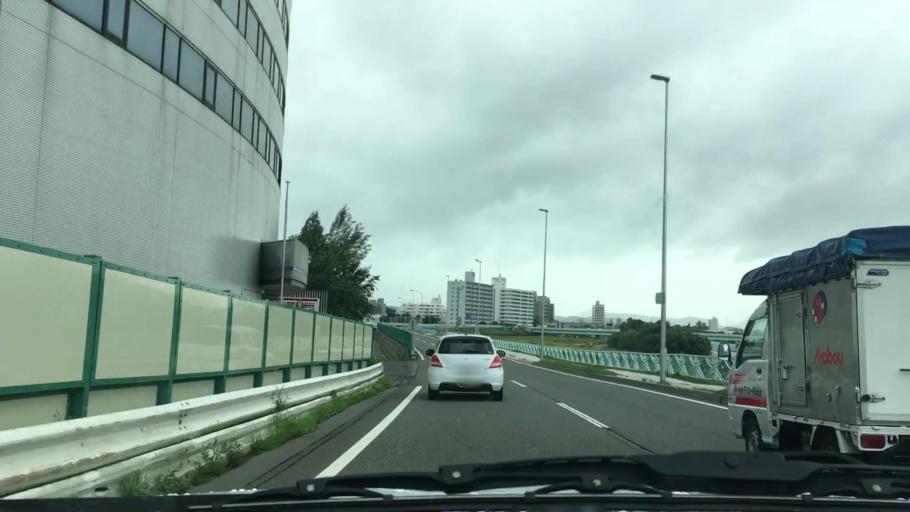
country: JP
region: Hokkaido
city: Sapporo
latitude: 43.0345
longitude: 141.3570
